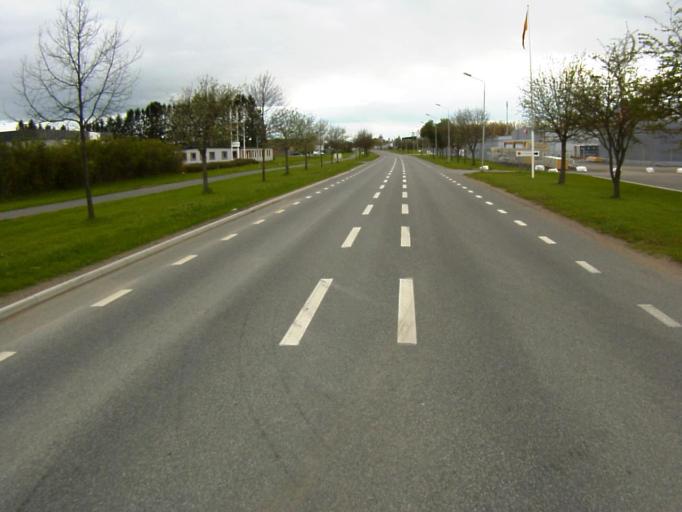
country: SE
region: Skane
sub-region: Kristianstads Kommun
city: Kristianstad
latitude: 56.0558
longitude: 14.1682
